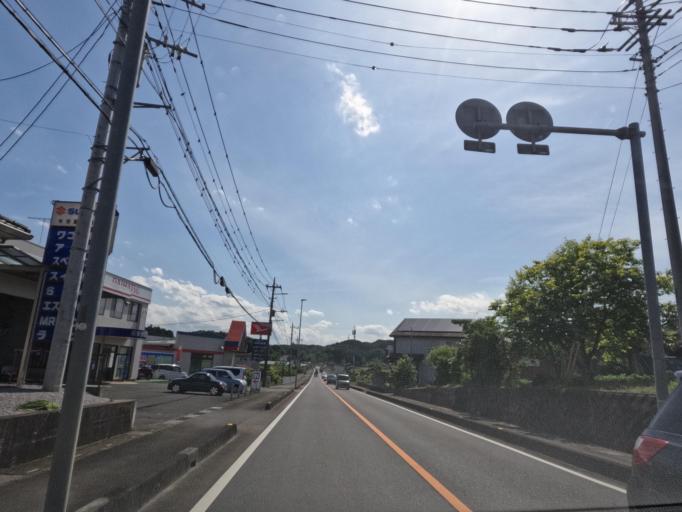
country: JP
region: Saitama
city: Ogawa
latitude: 36.0967
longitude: 139.3078
